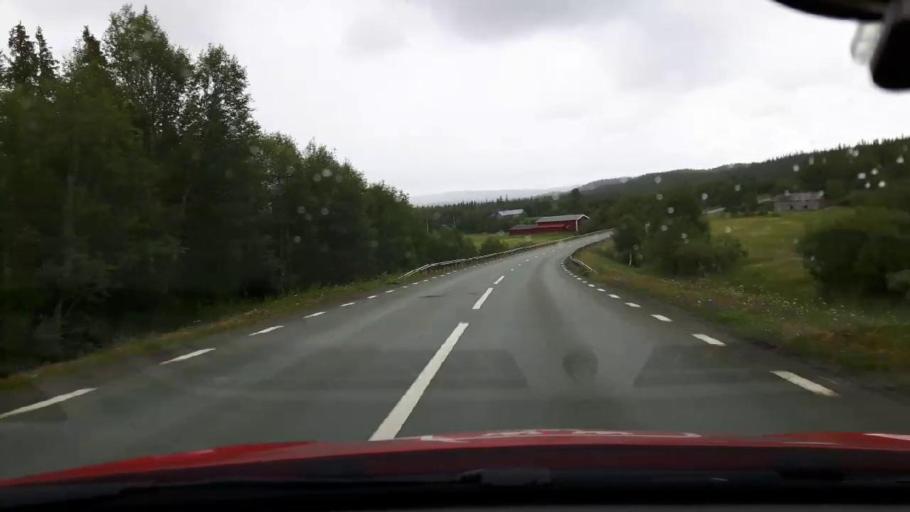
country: NO
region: Nord-Trondelag
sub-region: Meraker
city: Meraker
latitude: 63.2643
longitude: 12.2171
